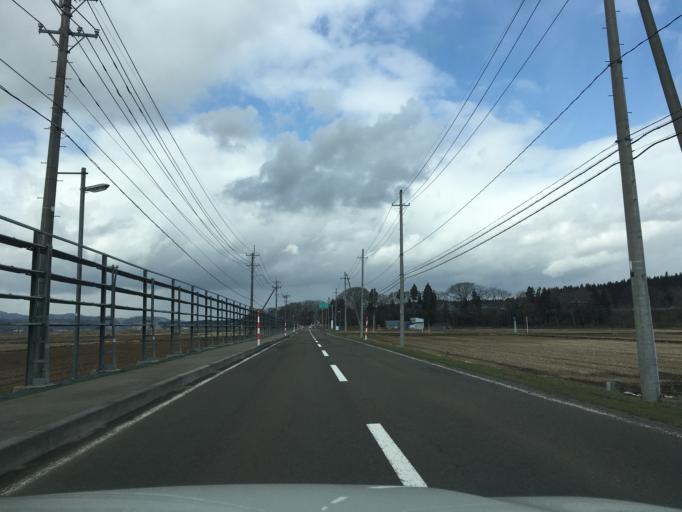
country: JP
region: Akita
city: Takanosu
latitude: 40.1396
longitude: 140.3511
